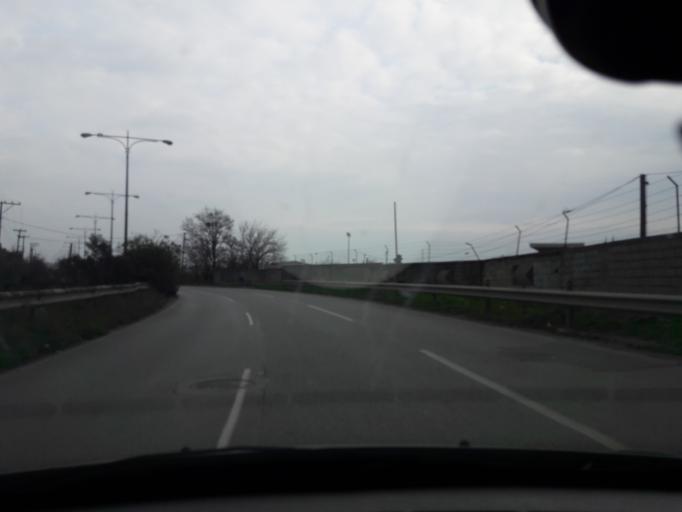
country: GR
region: Central Macedonia
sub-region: Nomos Thessalonikis
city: Menemeni
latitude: 40.6497
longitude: 22.9026
